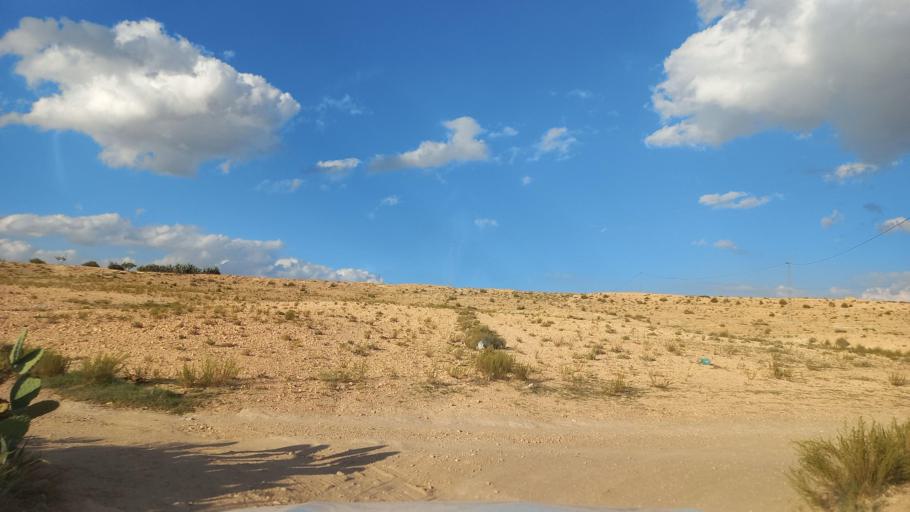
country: TN
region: Al Qasrayn
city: Sbiba
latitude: 35.3871
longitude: 9.0579
